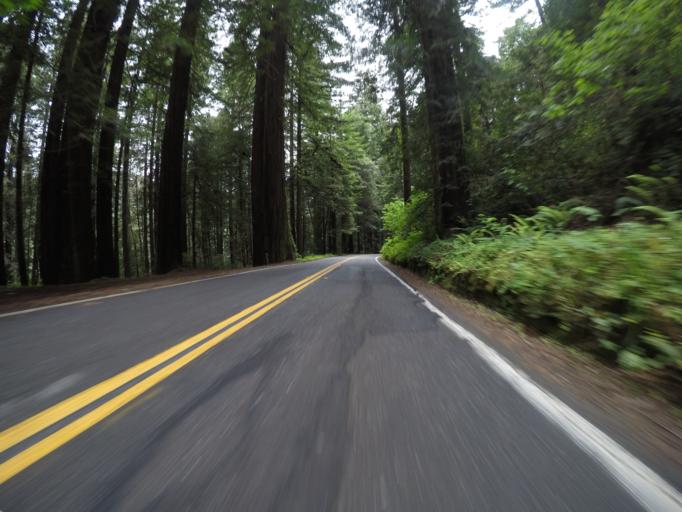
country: US
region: California
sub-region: Humboldt County
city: Rio Dell
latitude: 40.3948
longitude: -123.9326
